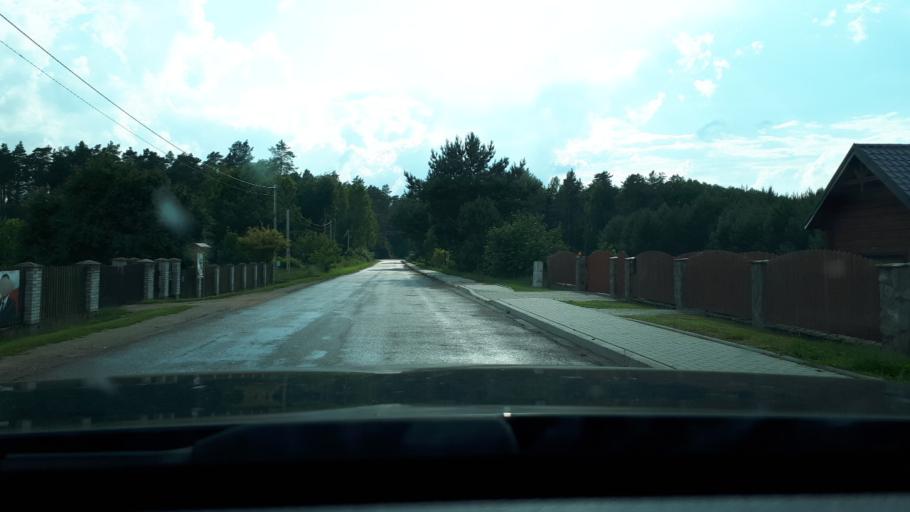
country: PL
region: Podlasie
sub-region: Powiat moniecki
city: Knyszyn
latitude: 53.2731
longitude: 22.9657
